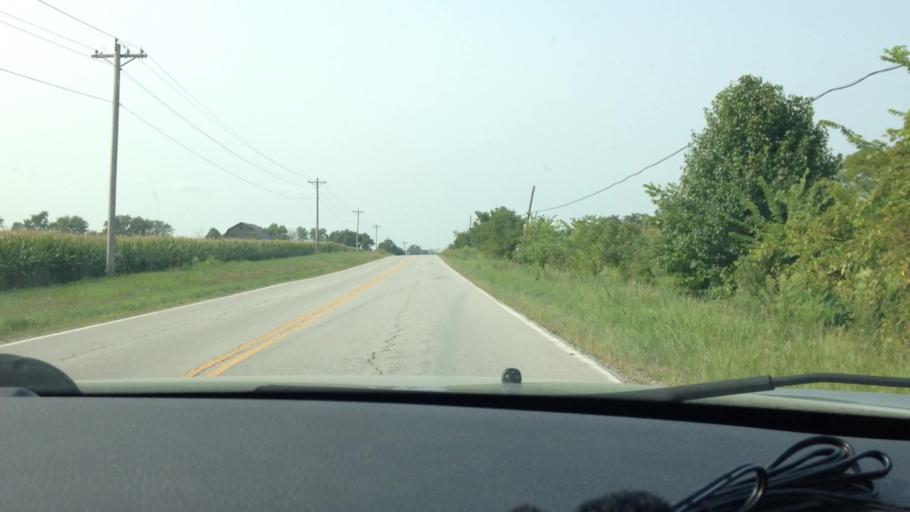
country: US
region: Missouri
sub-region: Platte County
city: Platte City
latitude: 39.4084
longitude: -94.7962
